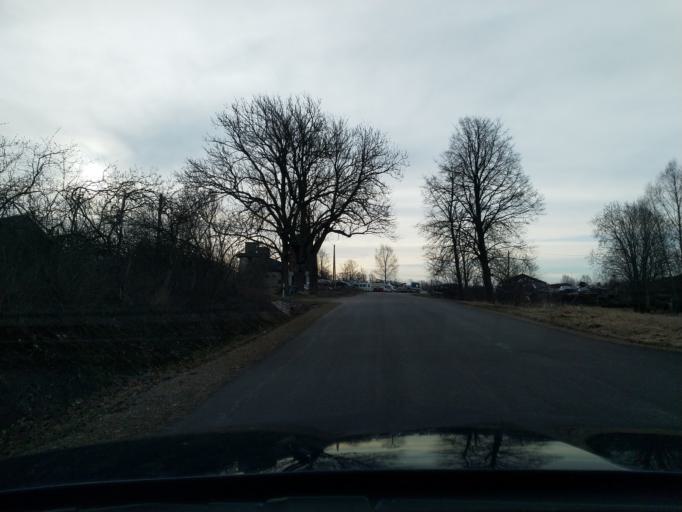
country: LV
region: Kuldigas Rajons
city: Kuldiga
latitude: 56.9604
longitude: 22.0085
